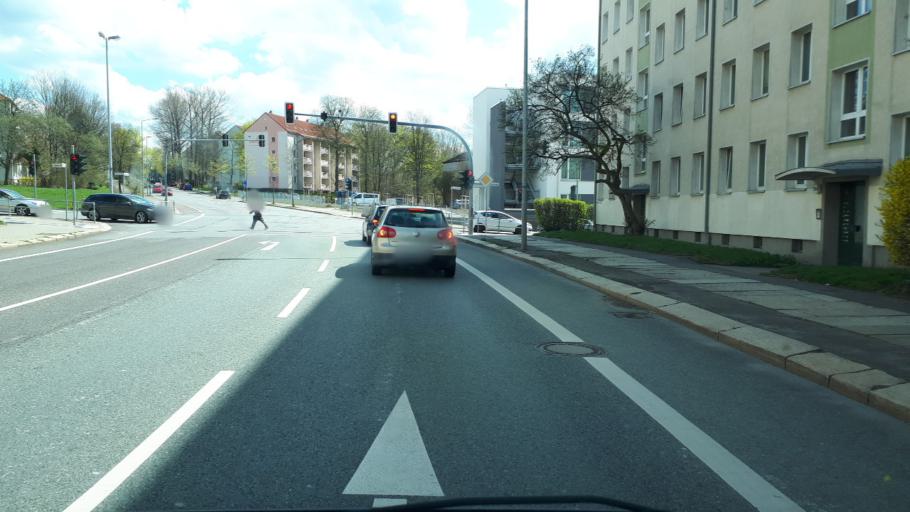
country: DE
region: Saxony
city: Chemnitz
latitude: 50.8239
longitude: 12.9317
